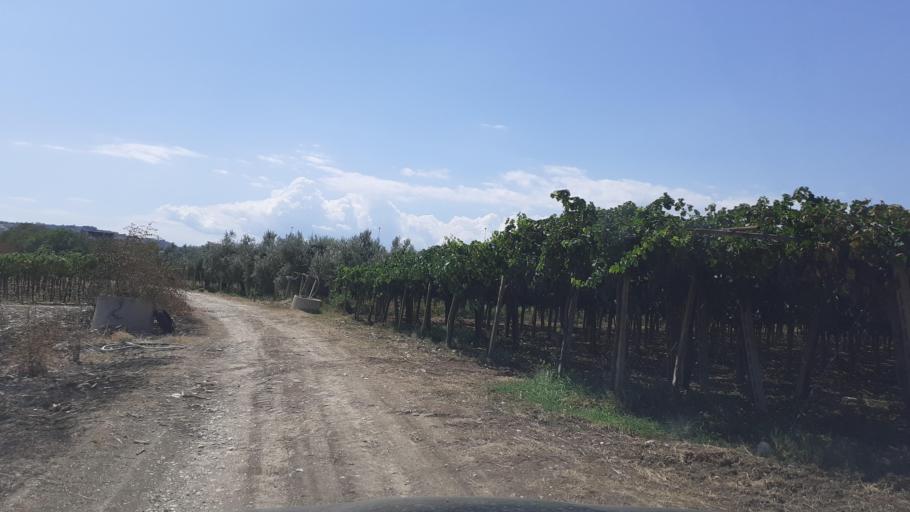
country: IT
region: Abruzzo
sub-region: Provincia di Chieti
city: Fossacesia
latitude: 42.2113
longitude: 14.4951
